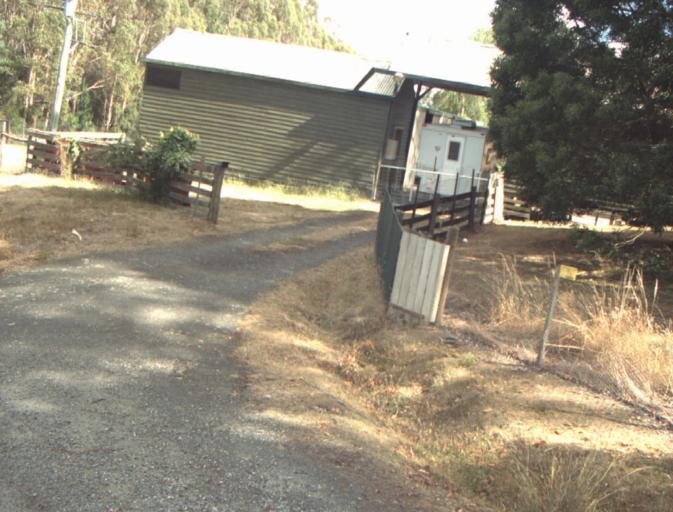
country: AU
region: Tasmania
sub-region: Launceston
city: Mayfield
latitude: -41.2750
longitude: 147.2190
